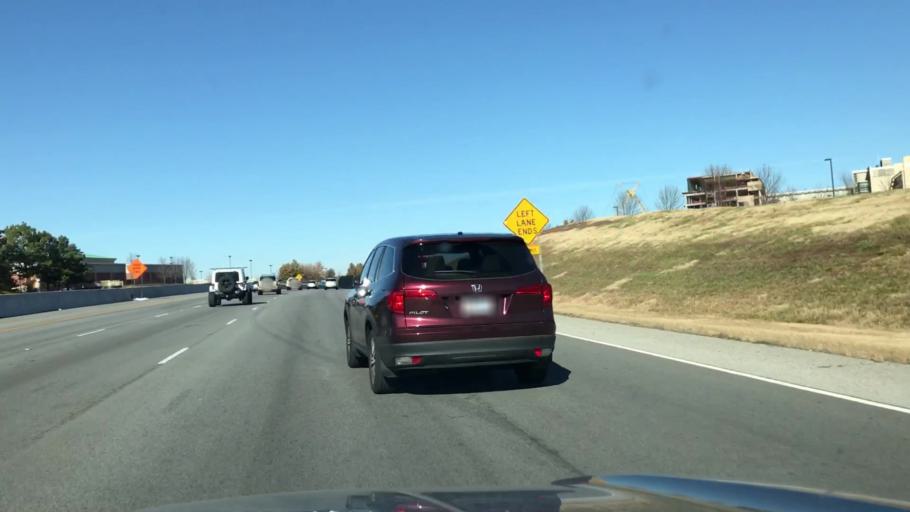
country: US
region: Arkansas
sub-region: Benton County
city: Cave Springs
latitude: 36.3053
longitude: -94.1834
